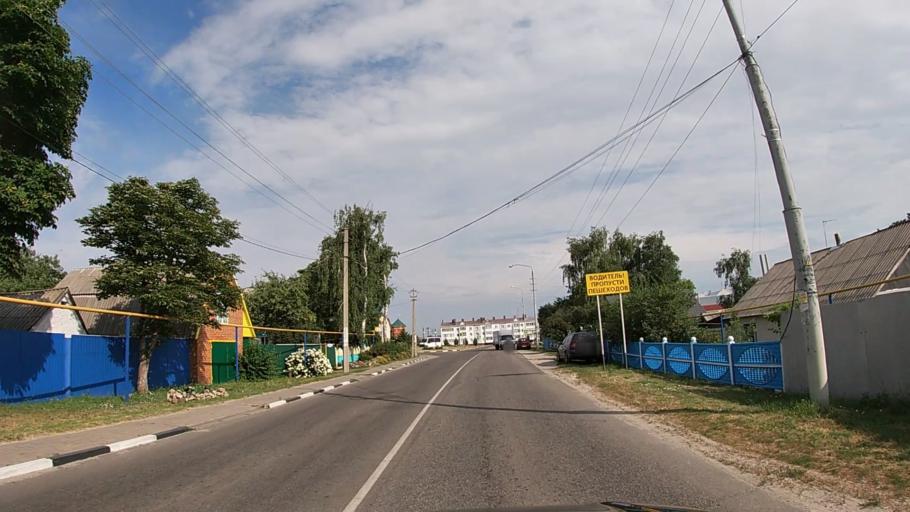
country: RU
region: Belgorod
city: Krasnaya Yaruga
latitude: 50.8009
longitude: 35.6607
